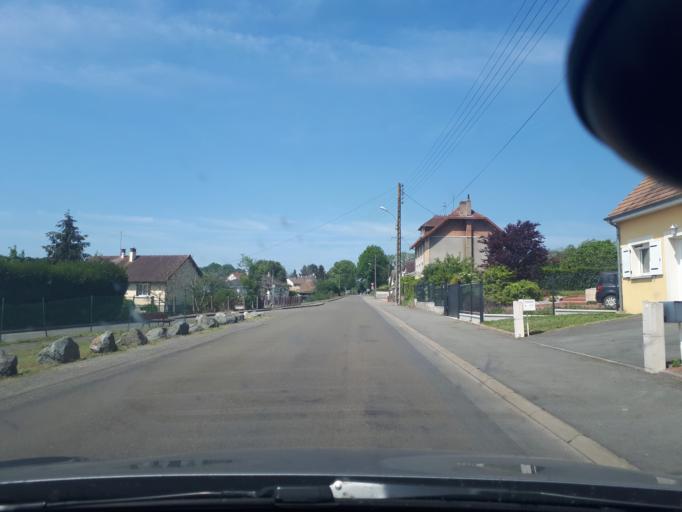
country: FR
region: Pays de la Loire
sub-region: Departement de la Sarthe
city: Montfort-le-Gesnois
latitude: 48.0504
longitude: 0.3998
